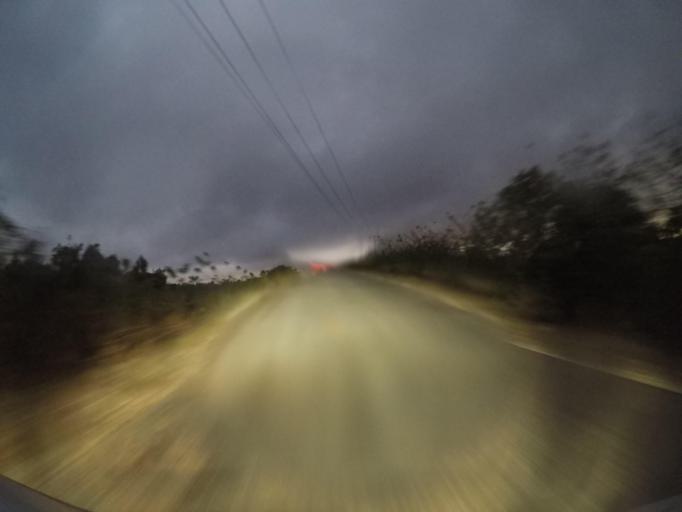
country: TL
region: Lautem
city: Lospalos
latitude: -8.4199
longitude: 127.0050
